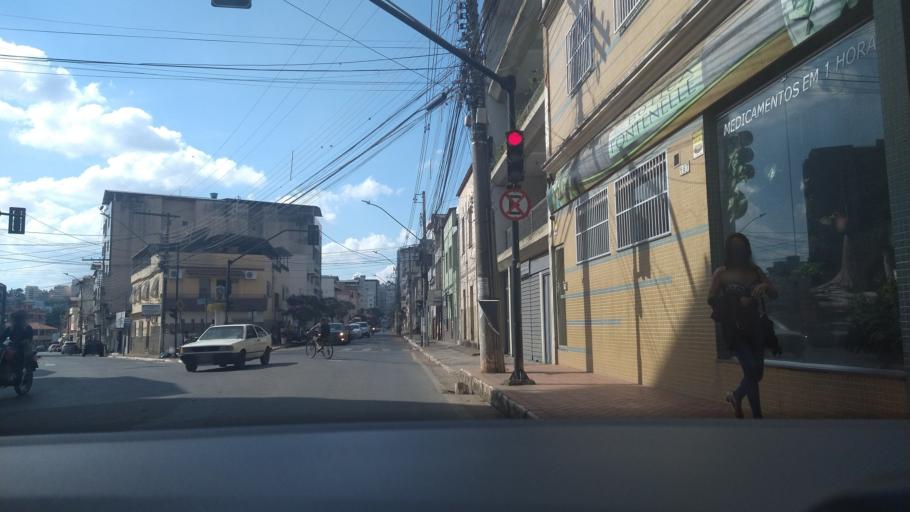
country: BR
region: Minas Gerais
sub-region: Vicosa
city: Vicosa
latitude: -20.7616
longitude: -42.8802
